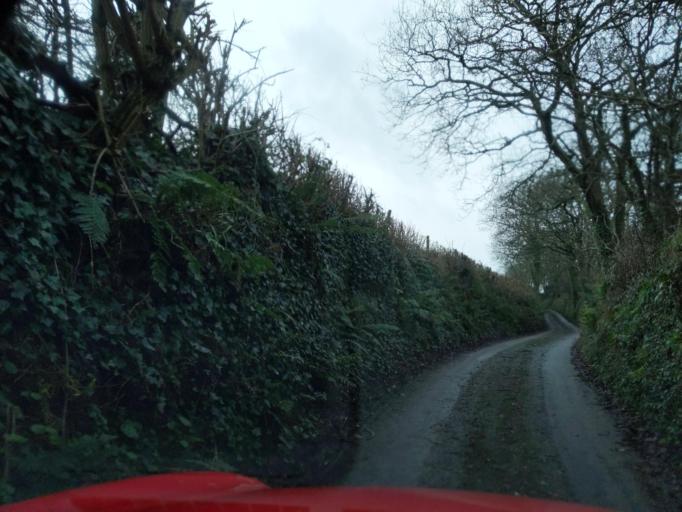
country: GB
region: England
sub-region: Cornwall
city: Duloe
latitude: 50.3459
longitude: -4.5261
